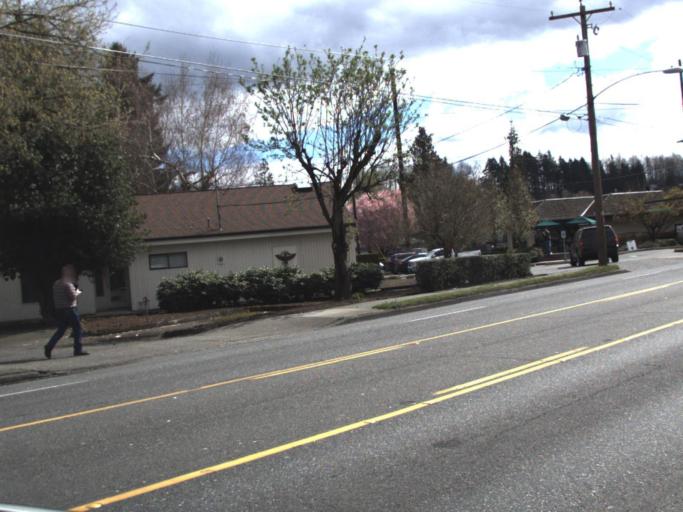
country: US
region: Washington
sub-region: King County
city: Auburn
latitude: 47.2950
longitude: -122.2145
